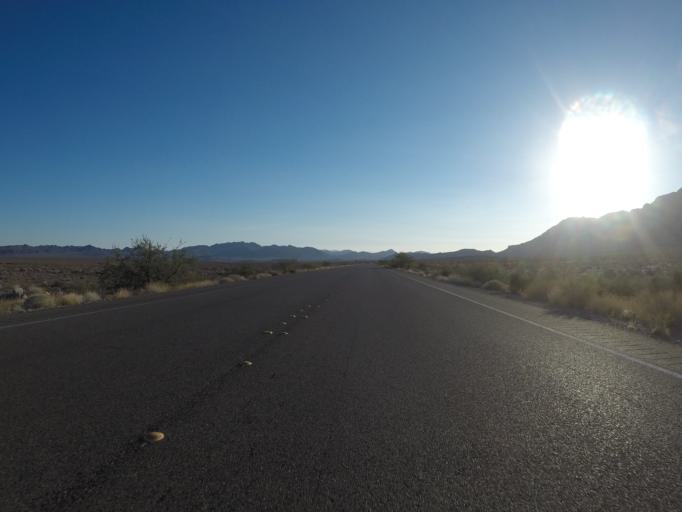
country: US
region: Nevada
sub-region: Clark County
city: Moapa Valley
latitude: 36.3414
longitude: -114.4880
